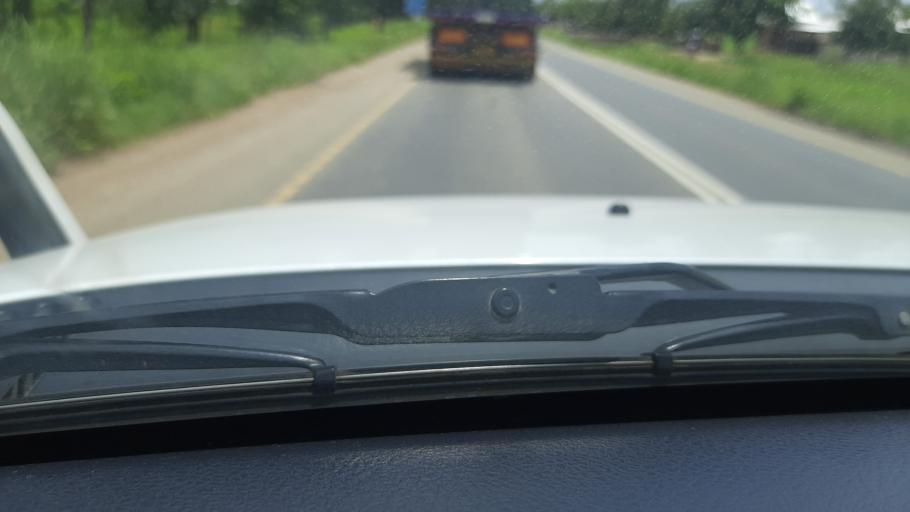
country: TZ
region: Pwani
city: Chalinze
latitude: -6.6370
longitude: 38.3403
